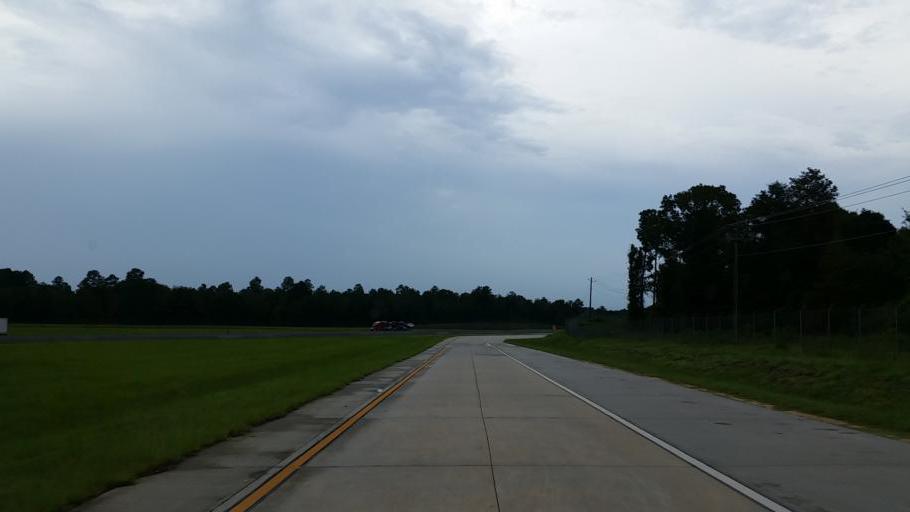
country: US
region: Georgia
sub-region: Tift County
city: Unionville
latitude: 31.3602
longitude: -83.4891
